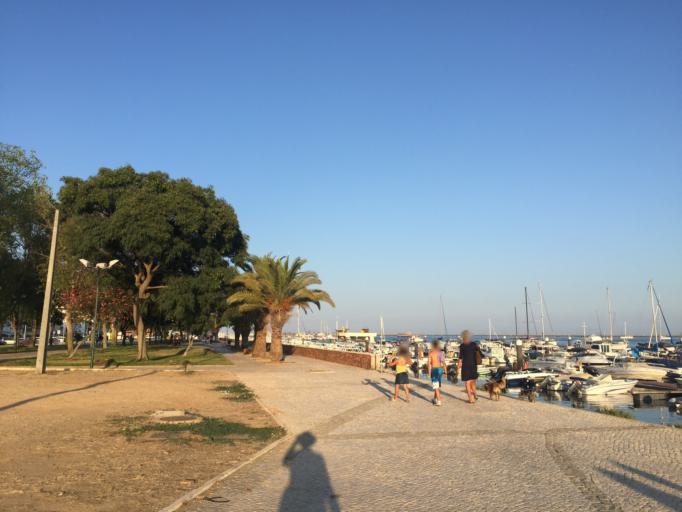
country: PT
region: Faro
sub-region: Olhao
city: Olhao
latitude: 37.0233
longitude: -7.8453
